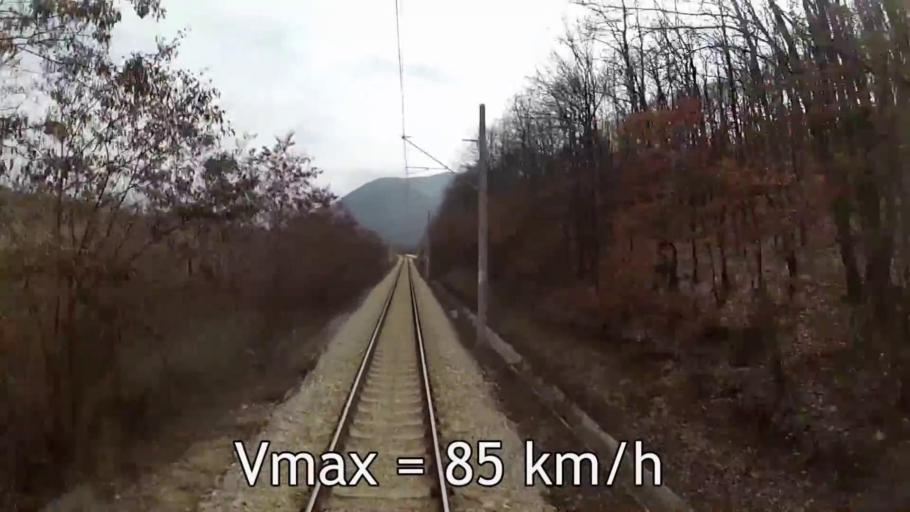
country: BG
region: Sofiya
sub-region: Obshtina Gorna Malina
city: Gorna Malina
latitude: 42.6893
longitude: 23.8330
